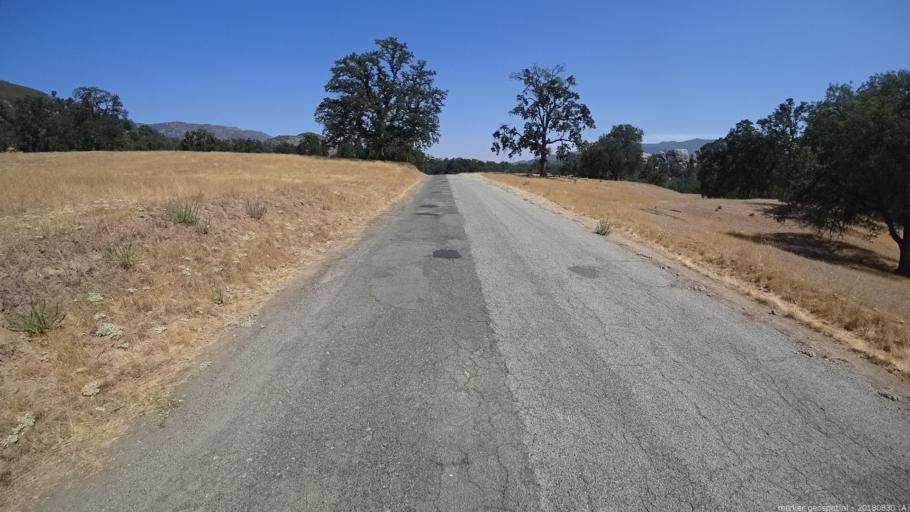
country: US
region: California
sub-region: Monterey County
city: Greenfield
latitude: 36.0881
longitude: -121.4082
